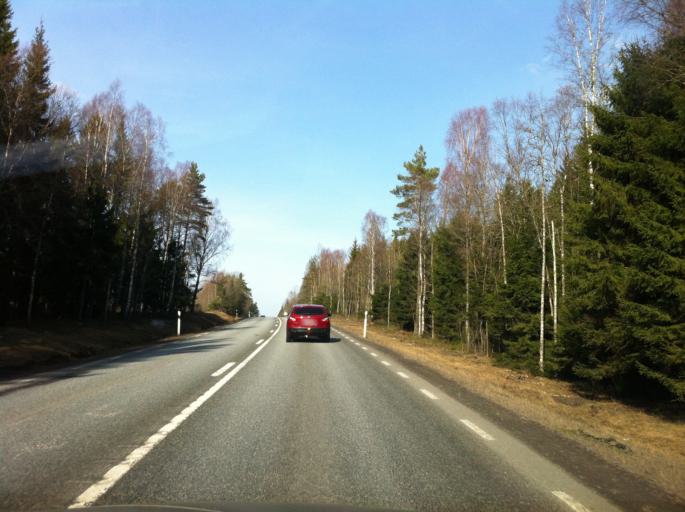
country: SE
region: Joenkoeping
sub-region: Mullsjo Kommun
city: Mullsjoe
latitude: 58.0098
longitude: 13.8308
